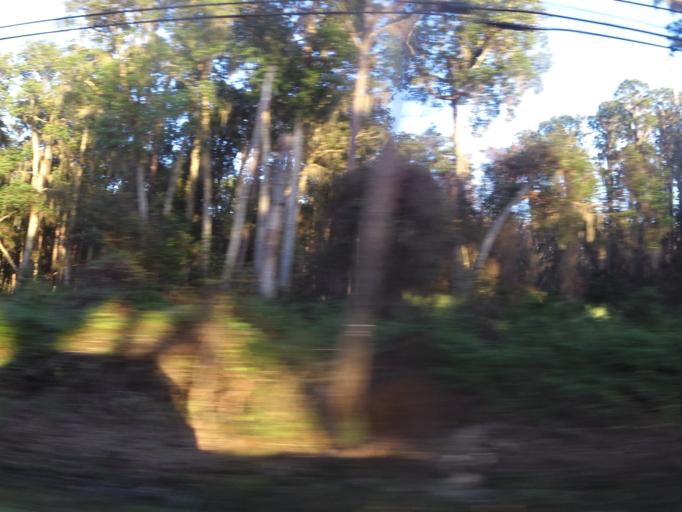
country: US
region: Florida
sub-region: Putnam County
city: East Palatka
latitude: 29.8304
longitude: -81.5534
